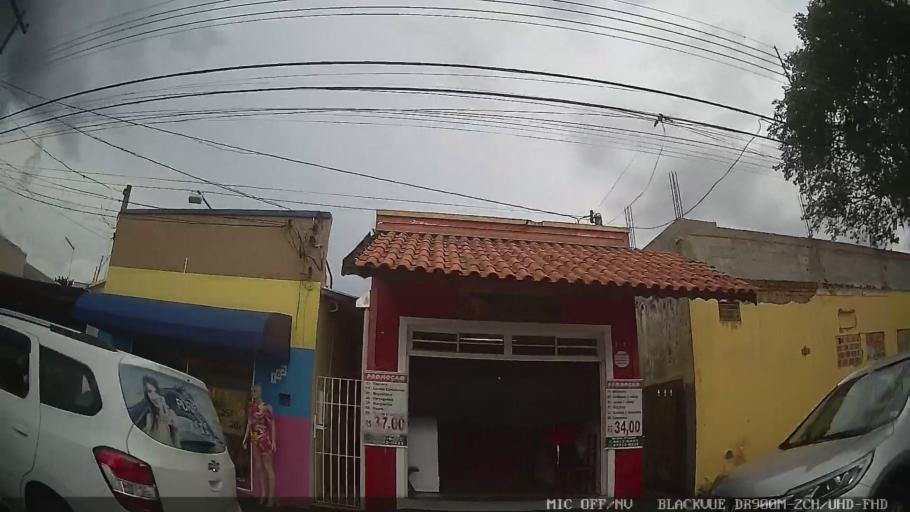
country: BR
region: Sao Paulo
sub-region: Atibaia
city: Atibaia
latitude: -23.1148
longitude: -46.5489
